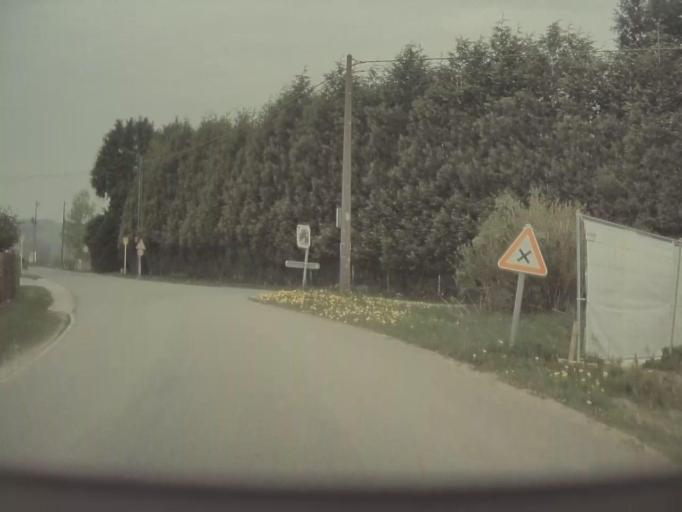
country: BE
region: Wallonia
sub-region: Province du Luxembourg
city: La Roche-en-Ardenne
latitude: 50.2316
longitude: 5.6171
